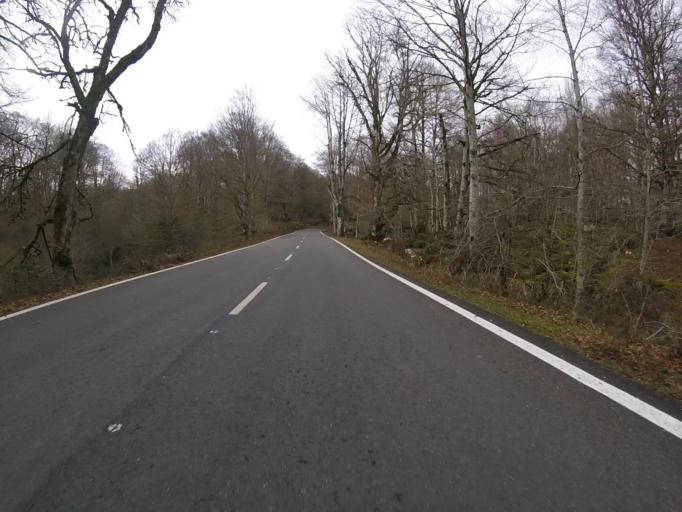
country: ES
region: Navarre
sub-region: Provincia de Navarra
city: Olazagutia
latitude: 42.8409
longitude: -2.1801
